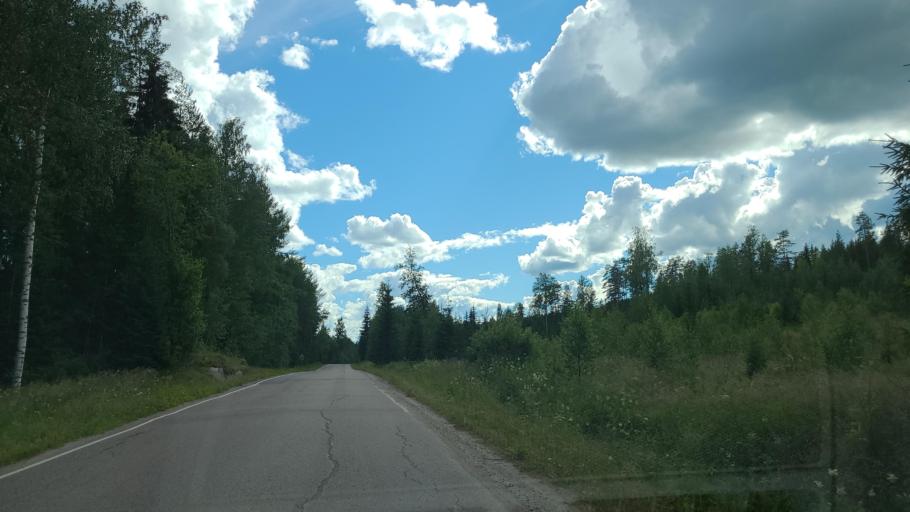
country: FI
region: Central Finland
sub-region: Jaemsae
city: Jaemsae
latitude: 61.9068
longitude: 25.2851
